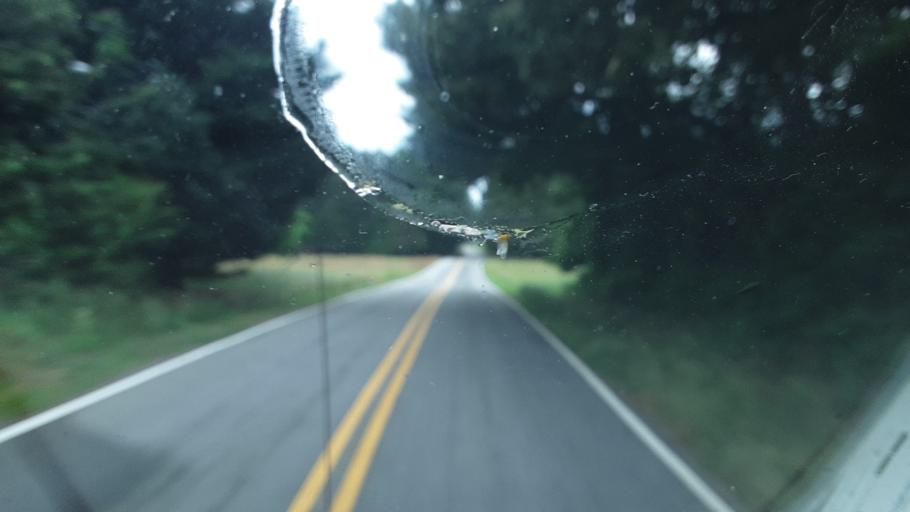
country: US
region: North Carolina
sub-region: Yadkin County
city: Jonesville
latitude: 36.0827
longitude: -80.8411
